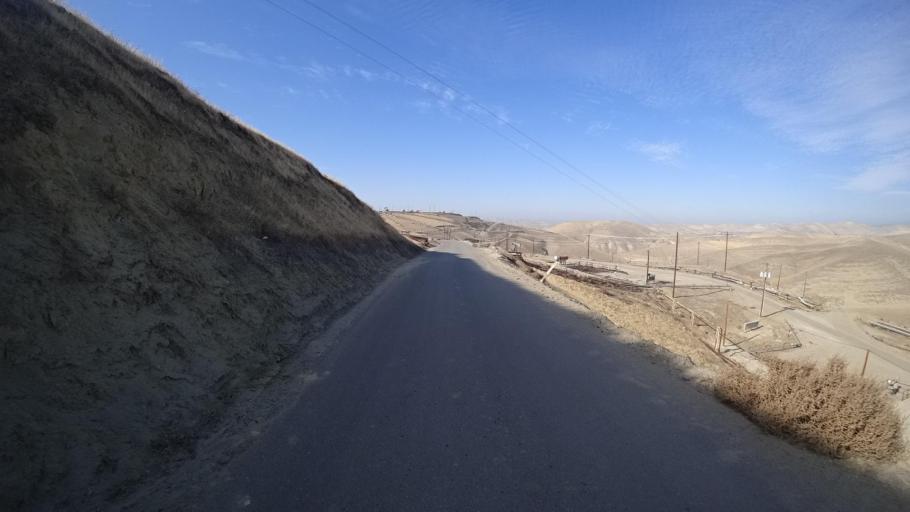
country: US
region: California
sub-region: Kern County
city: Oildale
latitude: 35.4891
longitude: -118.8898
